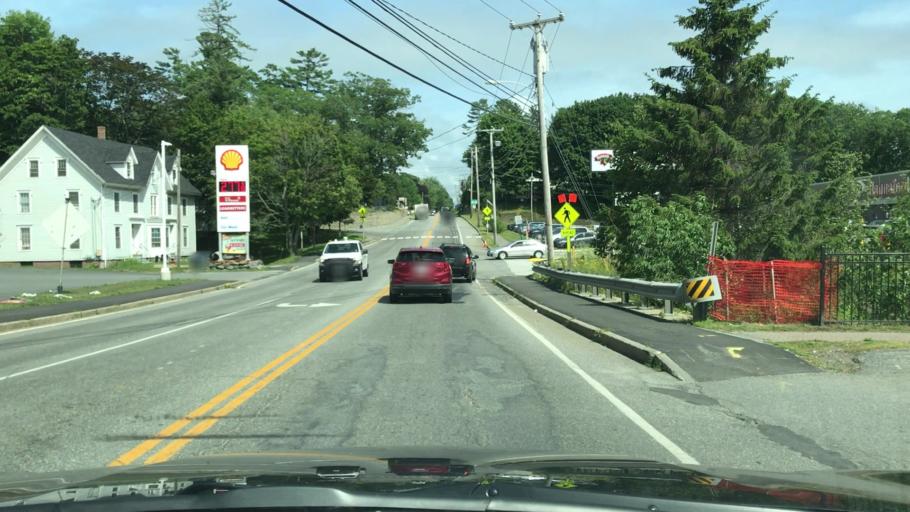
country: US
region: Maine
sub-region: Hancock County
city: Bucksport
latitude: 44.5711
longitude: -68.7865
